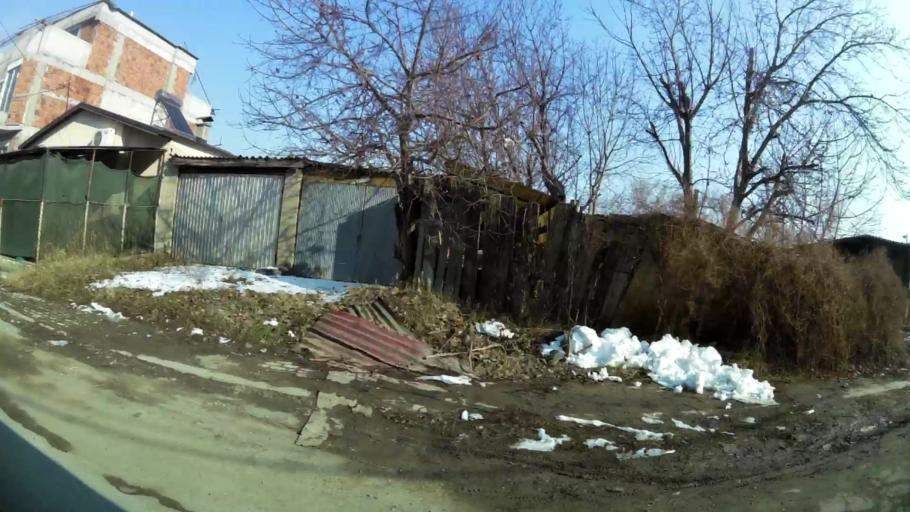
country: MK
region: Sopiste
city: Sopishte
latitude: 41.9750
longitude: 21.4350
